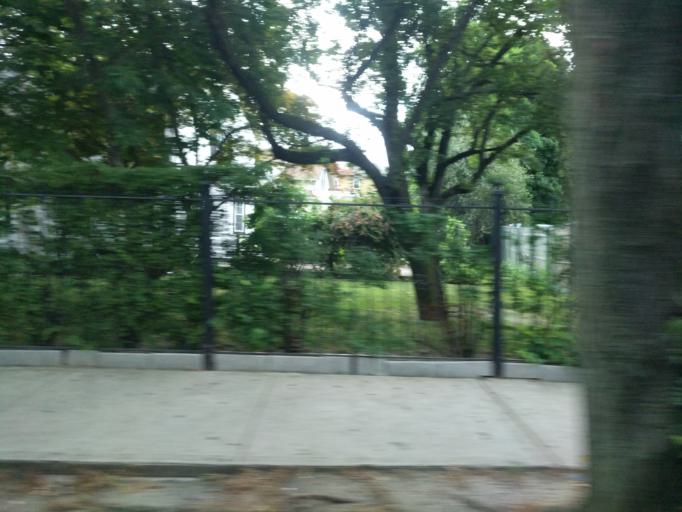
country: US
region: New York
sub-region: Nassau County
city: South Valley Stream
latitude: 40.6682
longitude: -73.7566
